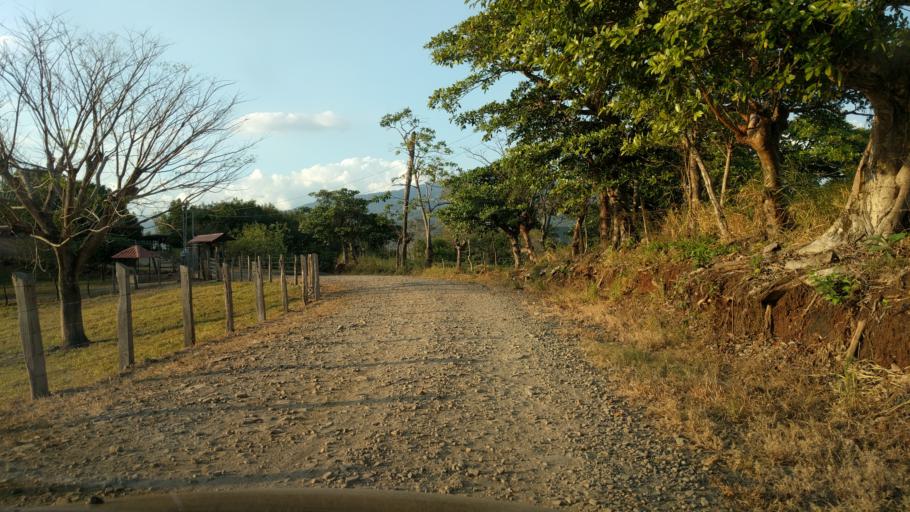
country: CR
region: Puntarenas
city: Esparza
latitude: 10.0300
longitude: -84.6977
